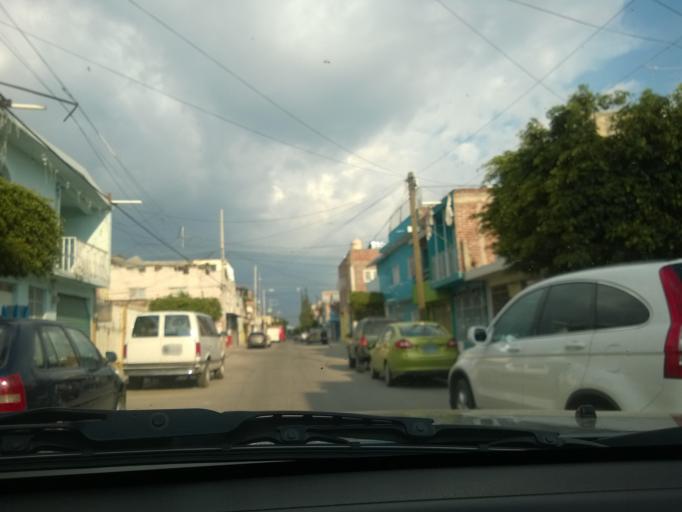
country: MX
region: Guanajuato
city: Leon
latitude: 21.1285
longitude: -101.6540
